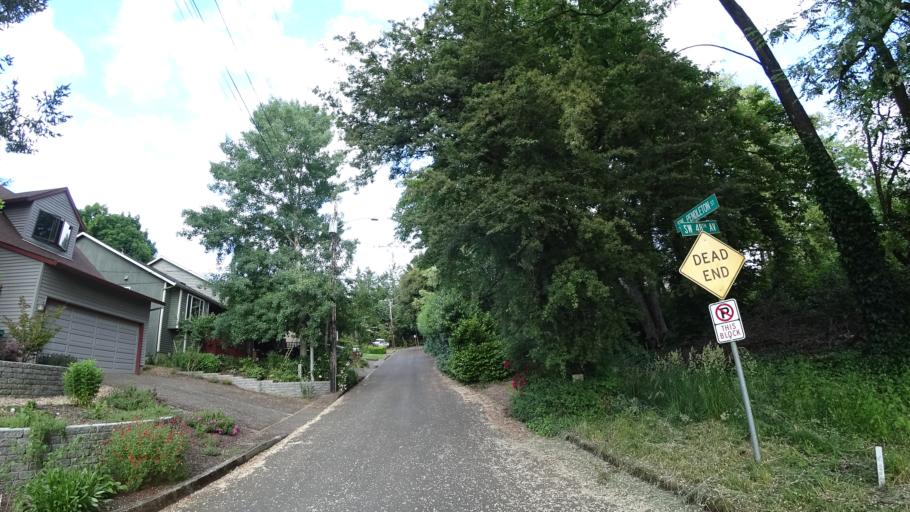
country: US
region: Oregon
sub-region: Washington County
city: Raleigh Hills
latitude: 45.4818
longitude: -122.7268
